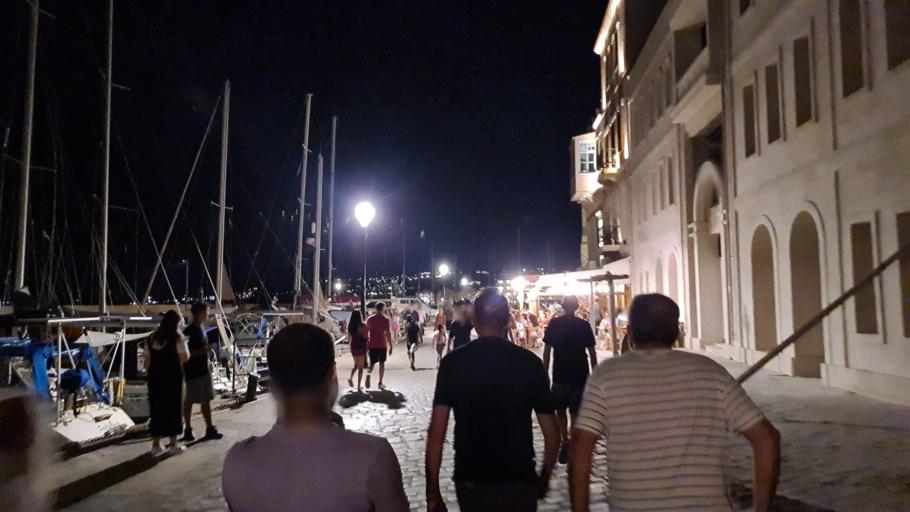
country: GR
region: Crete
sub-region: Nomos Chanias
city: Chania
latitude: 35.5186
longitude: 24.0190
